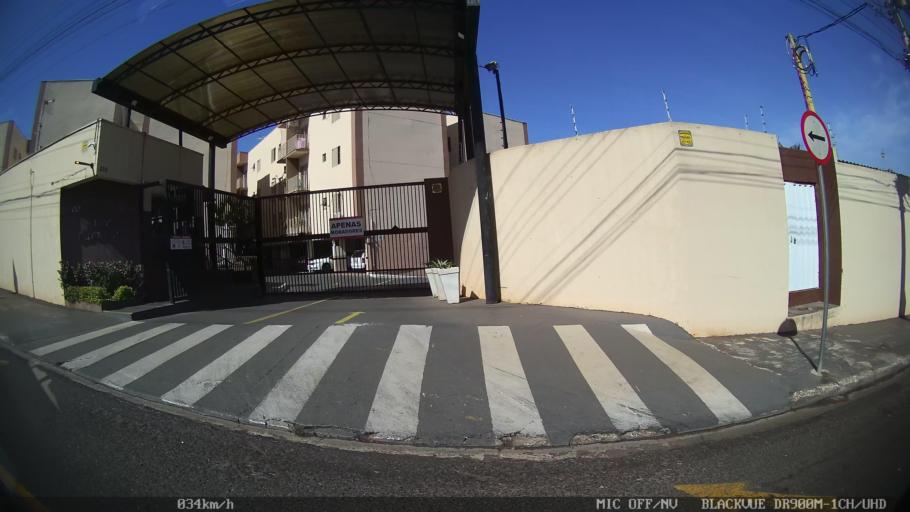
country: BR
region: Sao Paulo
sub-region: Sao Jose Do Rio Preto
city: Sao Jose do Rio Preto
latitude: -20.7820
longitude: -49.3792
